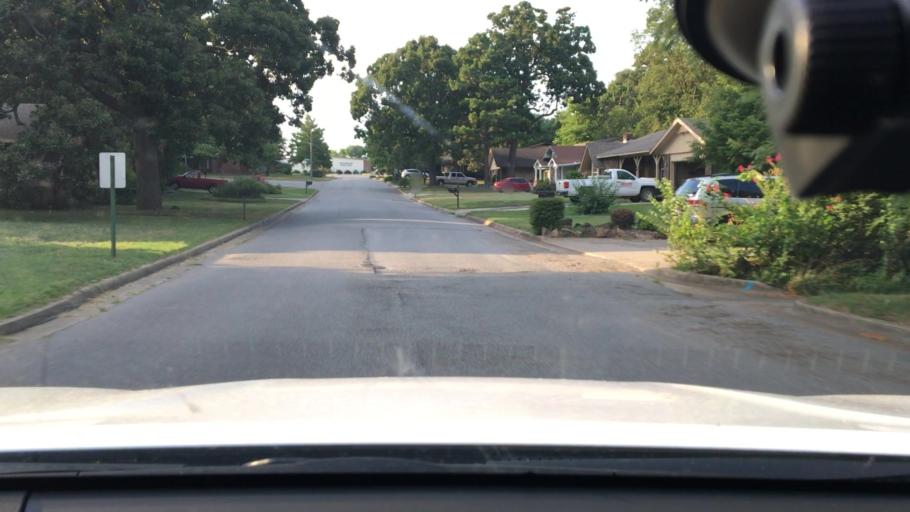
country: US
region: Arkansas
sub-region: Benton County
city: Rogers
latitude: 36.3394
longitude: -94.1620
